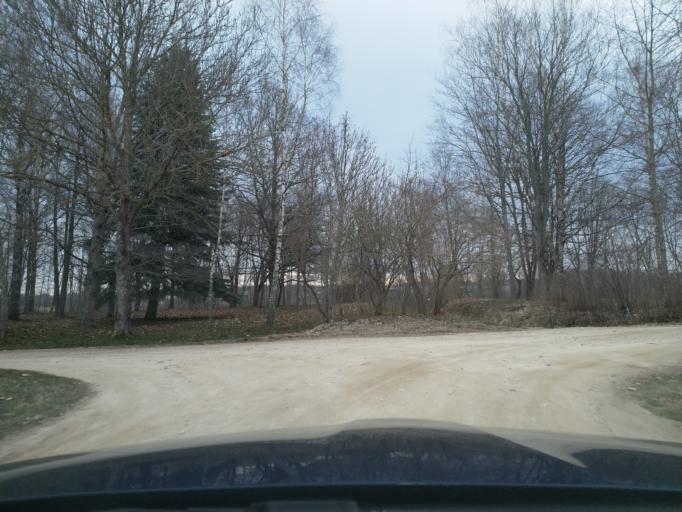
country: LV
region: Kuldigas Rajons
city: Kuldiga
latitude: 56.9540
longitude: 22.0003
